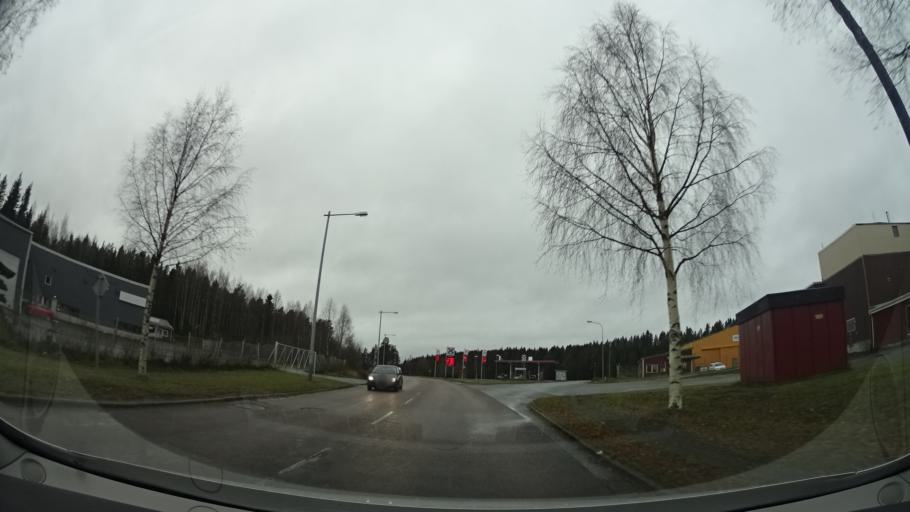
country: SE
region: Vaesterbotten
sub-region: Skelleftea Kommun
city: Skelleftea
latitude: 64.7617
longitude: 20.9497
